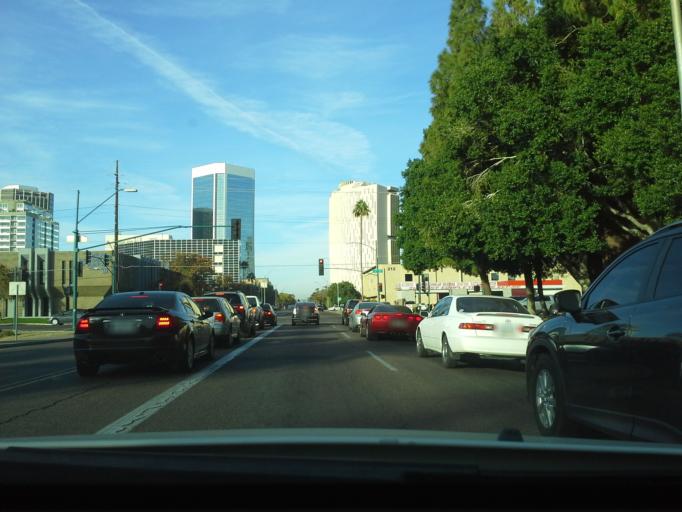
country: US
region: Arizona
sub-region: Maricopa County
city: Phoenix
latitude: 33.4875
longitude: -112.0687
